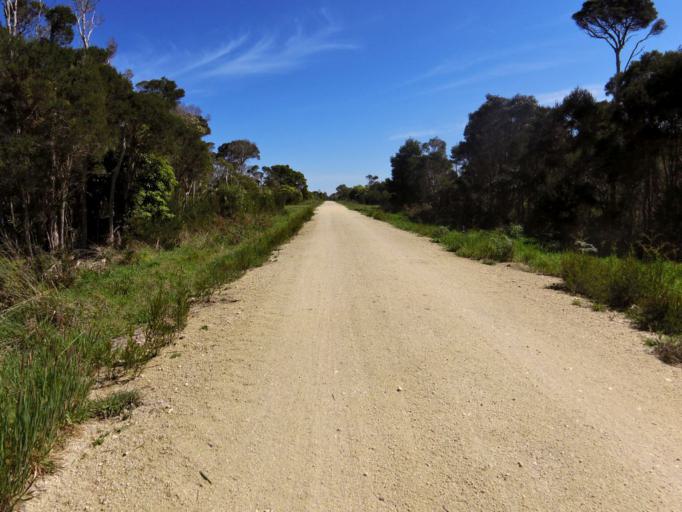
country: AU
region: Victoria
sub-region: Latrobe
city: Morwell
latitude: -38.6694
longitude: 146.4214
